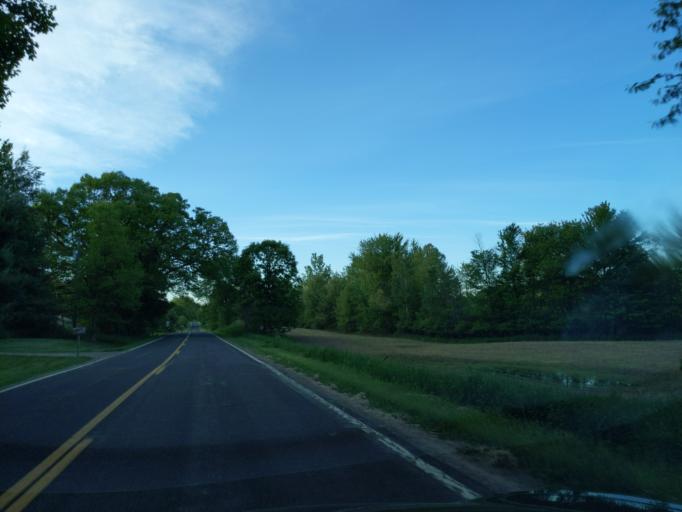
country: US
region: Michigan
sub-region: Ingham County
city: Stockbridge
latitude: 42.5273
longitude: -84.3025
